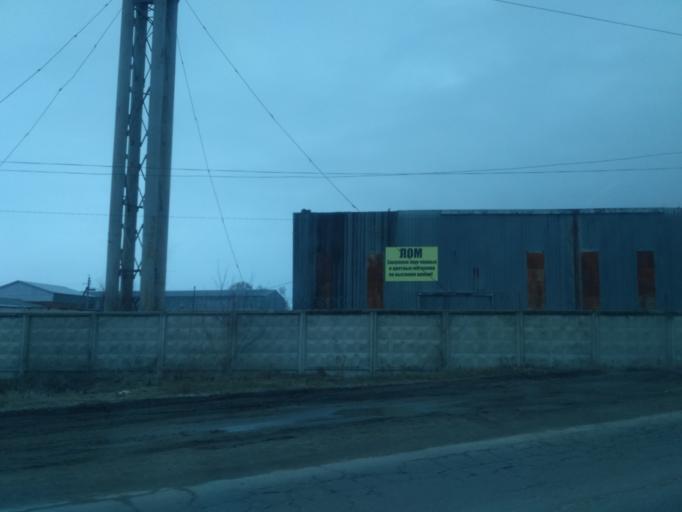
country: RU
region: Nizjnij Novgorod
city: Perevoz
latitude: 55.6023
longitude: 44.5594
